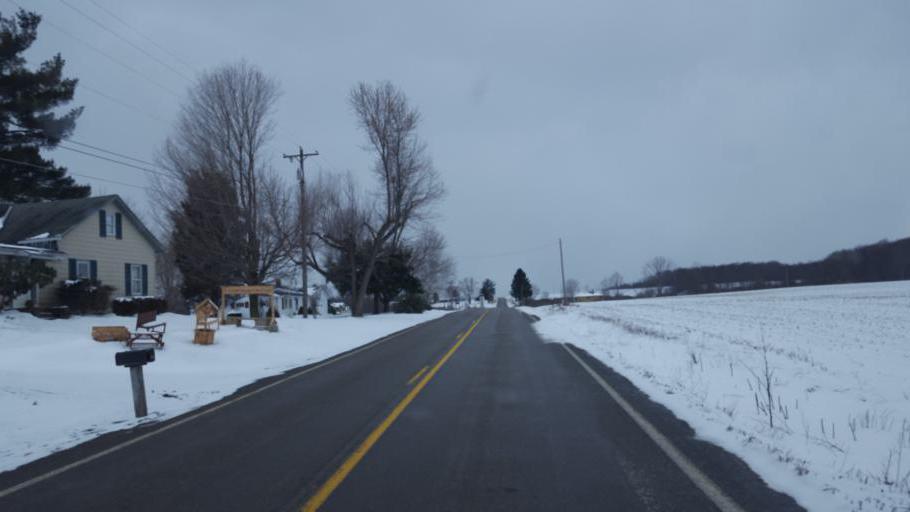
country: US
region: Pennsylvania
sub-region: Mercer County
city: Stoneboro
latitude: 41.4118
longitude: -80.0873
